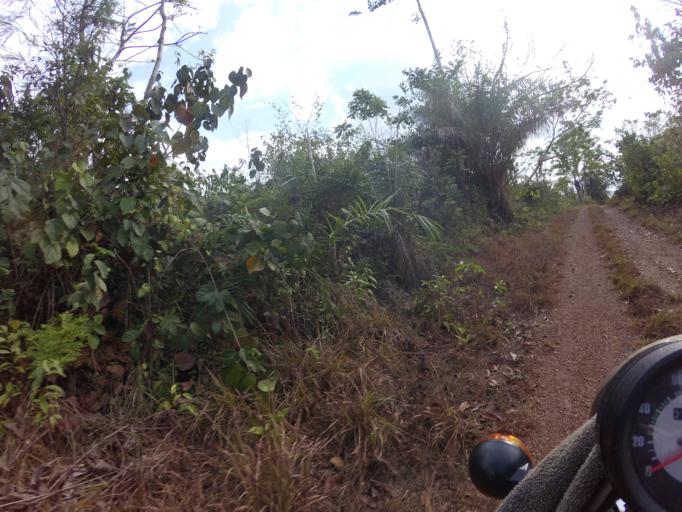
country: SL
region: Southern Province
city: Zimmi
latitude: 7.1488
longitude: -11.2027
